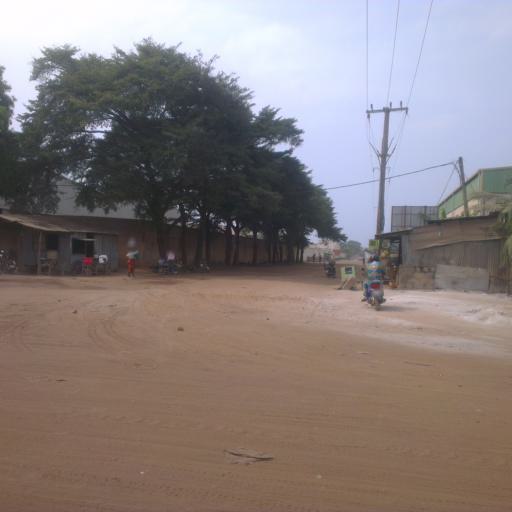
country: TG
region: Maritime
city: Lome
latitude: 6.1615
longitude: 1.2945
